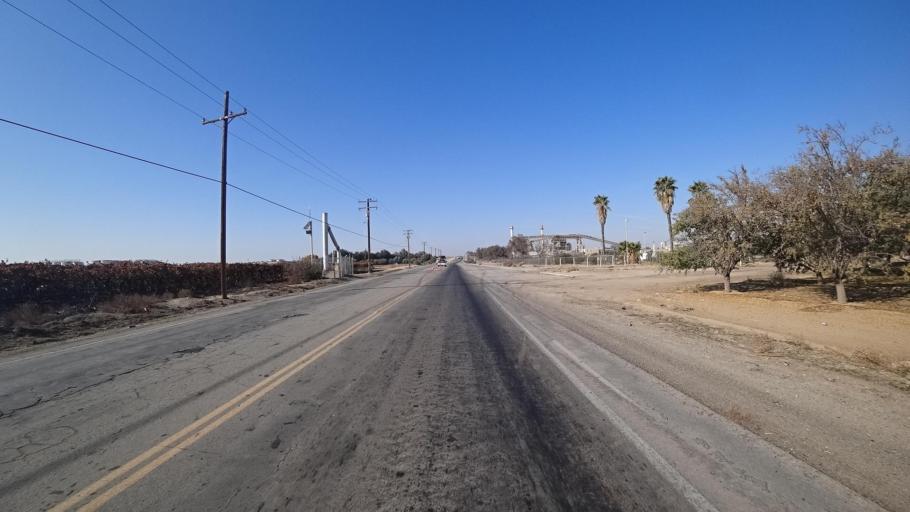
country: US
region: California
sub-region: Kern County
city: McFarland
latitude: 35.7180
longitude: -119.2294
